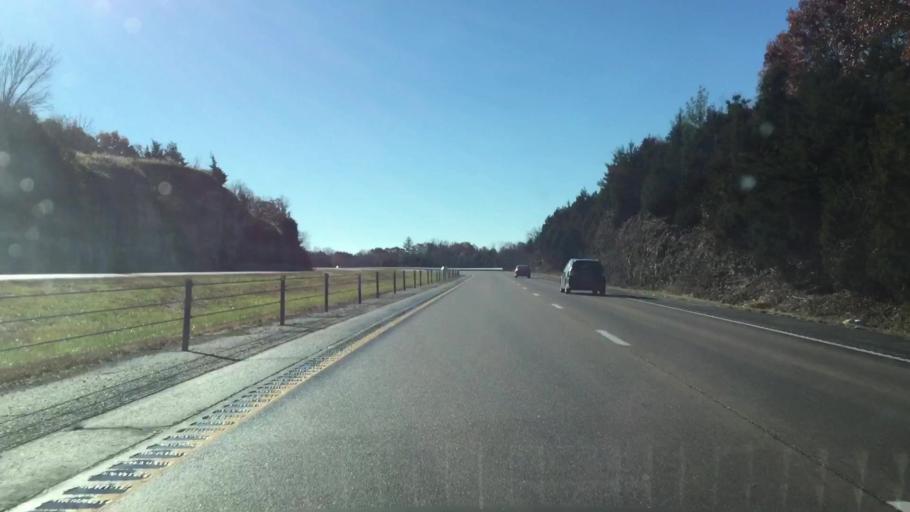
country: US
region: Missouri
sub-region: Boone County
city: Ashland
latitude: 38.6863
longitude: -92.2553
